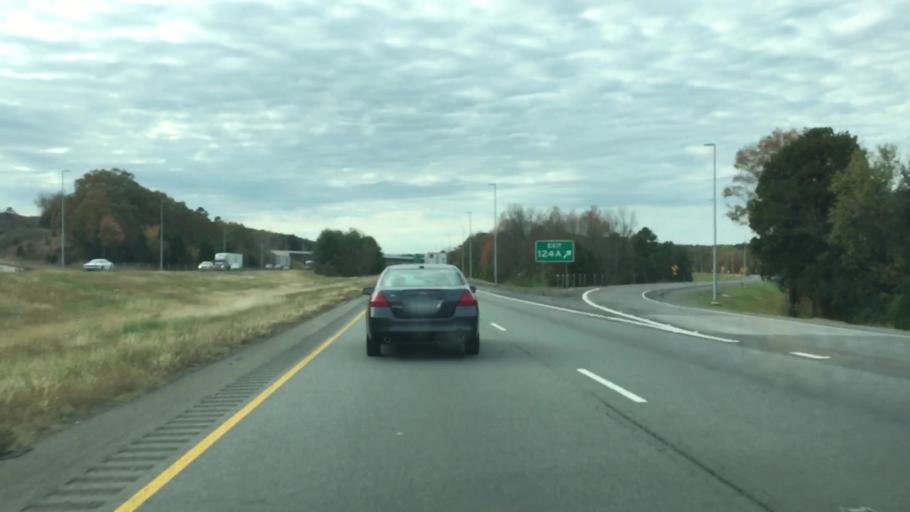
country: US
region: Arkansas
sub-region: Faulkner County
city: Conway
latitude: 35.1189
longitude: -92.4546
